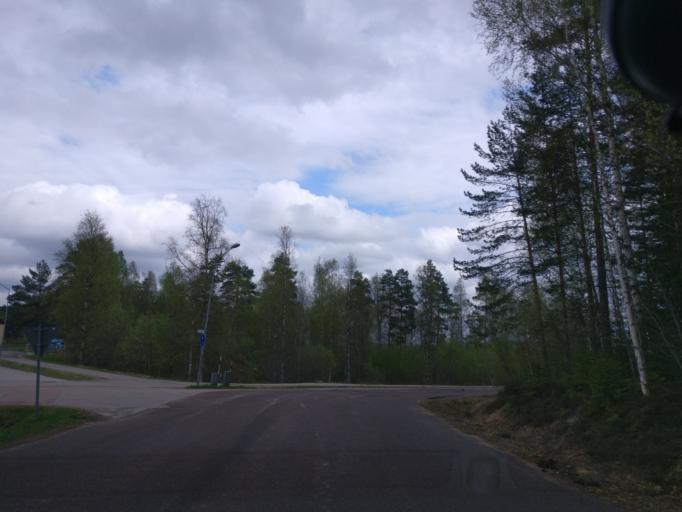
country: SE
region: Vaermland
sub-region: Hagfors Kommun
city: Ekshaerad
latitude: 60.1754
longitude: 13.4890
